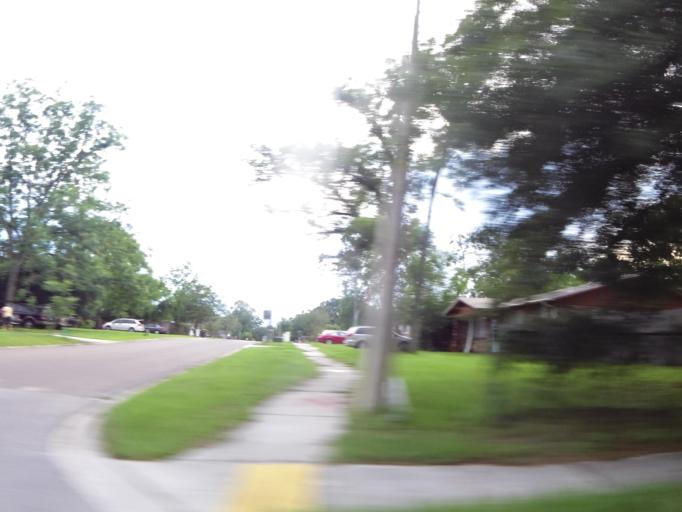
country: US
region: Florida
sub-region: Duval County
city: Jacksonville
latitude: 30.3071
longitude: -81.7835
